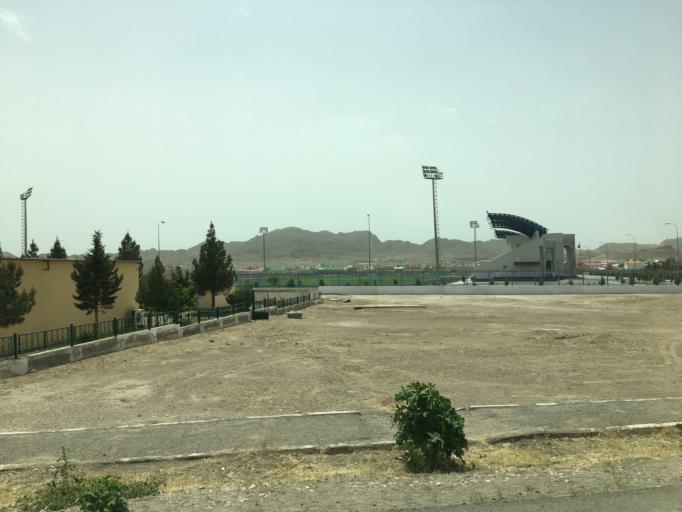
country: TM
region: Balkan
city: Turkmenbasy
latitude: 40.0119
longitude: 53.1175
